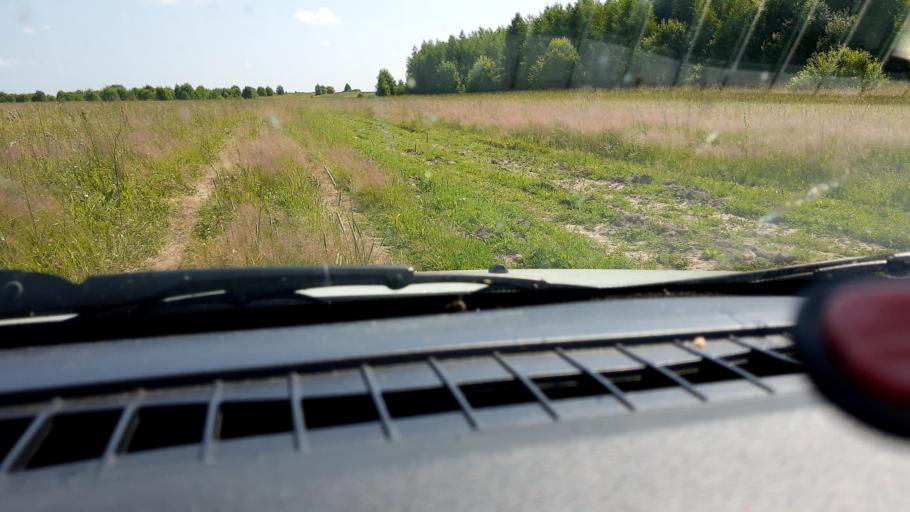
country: RU
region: Nizjnij Novgorod
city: Sharanga
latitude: 57.0455
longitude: 46.7254
